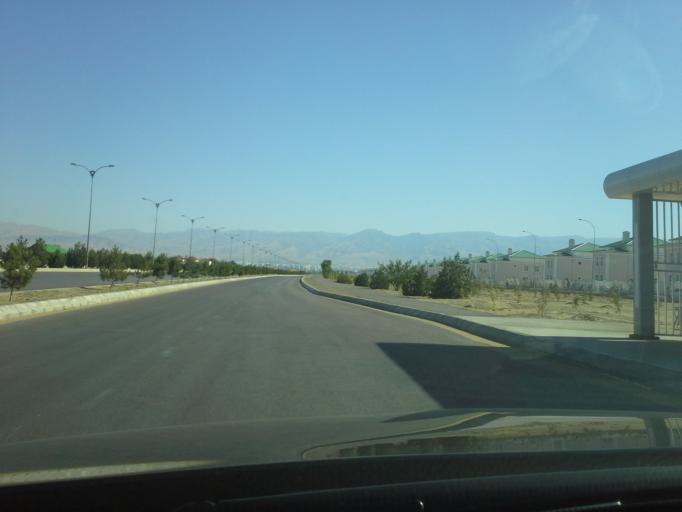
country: TM
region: Ahal
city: Ashgabat
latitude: 38.0230
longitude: 58.4056
